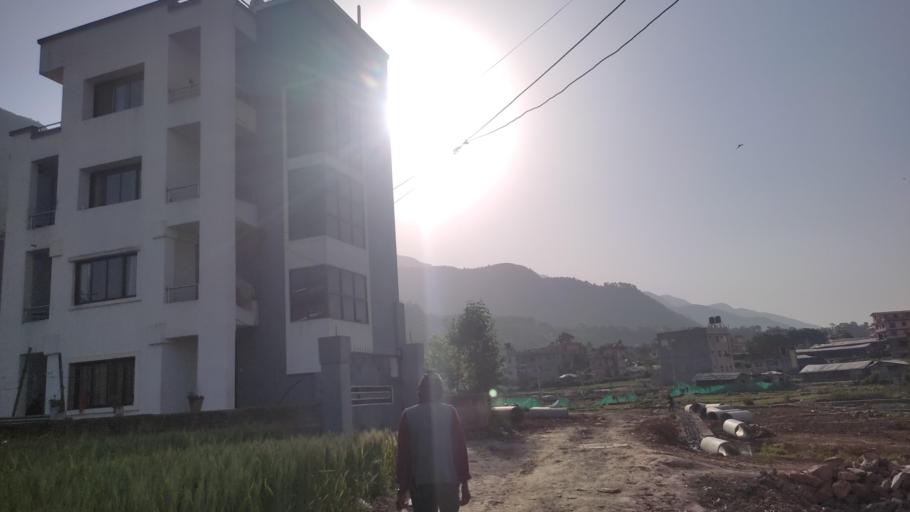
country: NP
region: Central Region
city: Kirtipur
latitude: 27.6602
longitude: 85.2684
